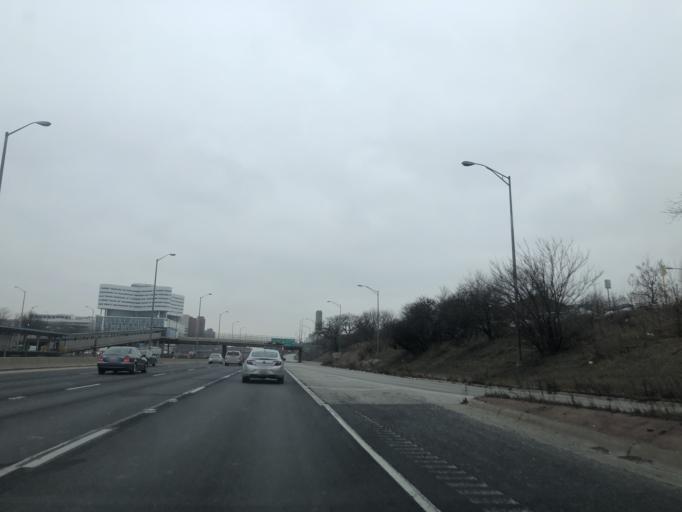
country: US
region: Illinois
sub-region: Cook County
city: Chicago
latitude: 41.8763
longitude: -87.6592
